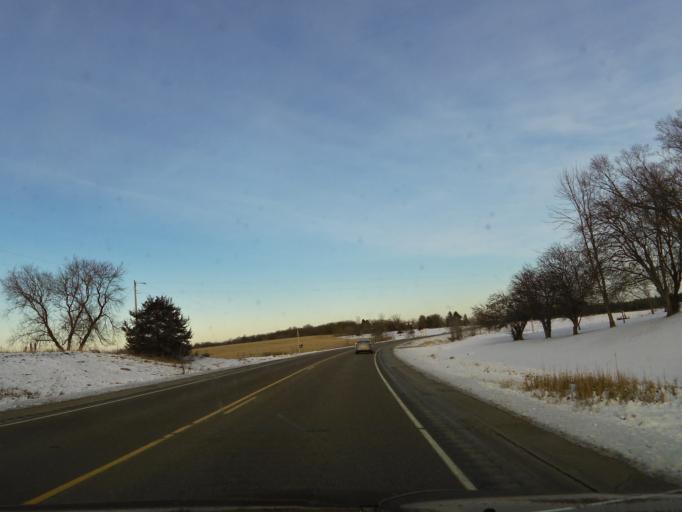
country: US
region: Wisconsin
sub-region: Polk County
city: Osceola
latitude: 45.3443
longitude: -92.7227
